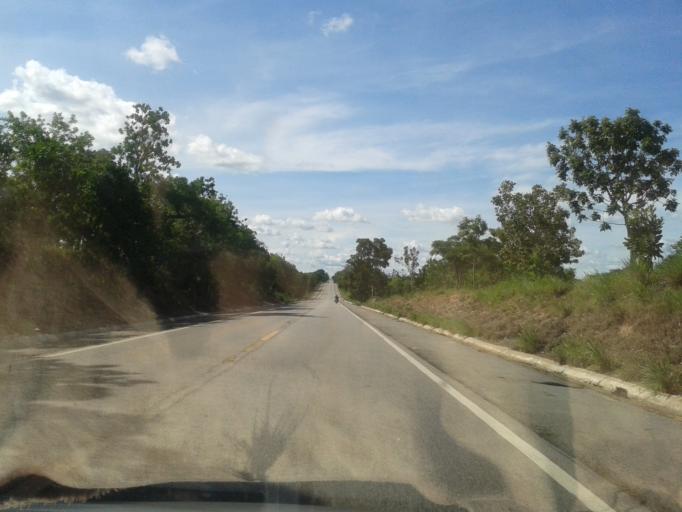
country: BR
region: Goias
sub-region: Mozarlandia
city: Mozarlandia
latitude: -15.2754
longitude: -50.4801
